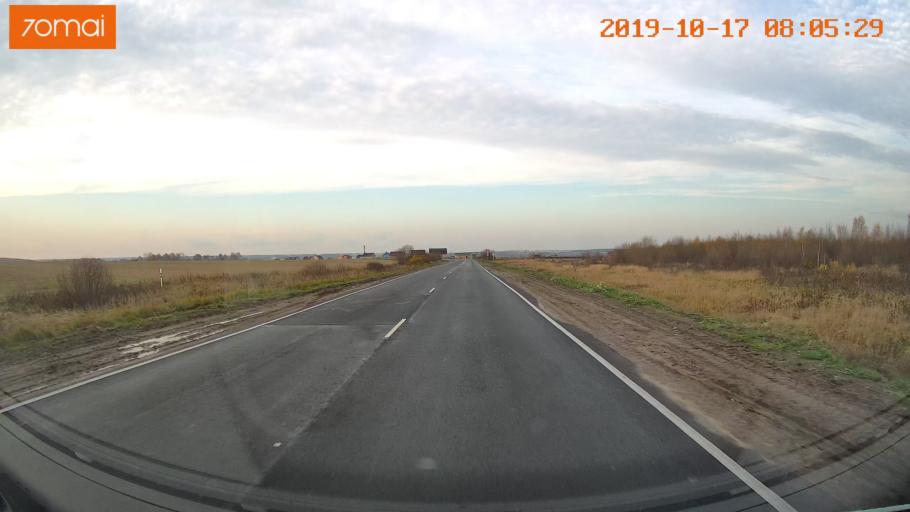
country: RU
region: Vladimir
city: Kol'chugino
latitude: 56.3341
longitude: 39.4146
